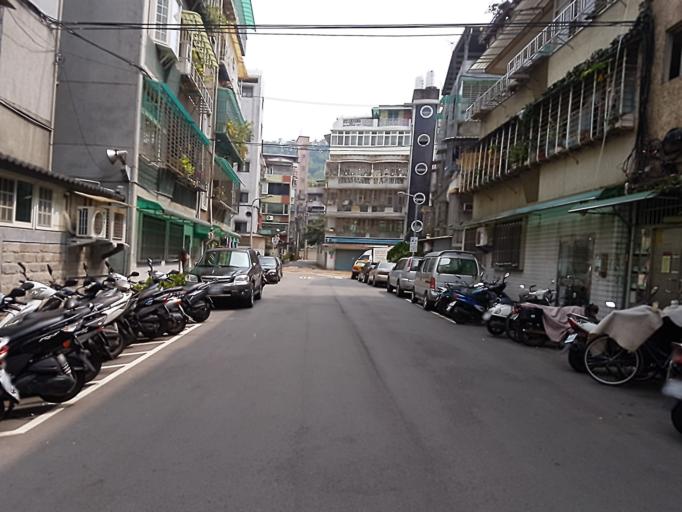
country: TW
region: Taipei
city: Taipei
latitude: 24.9967
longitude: 121.5464
